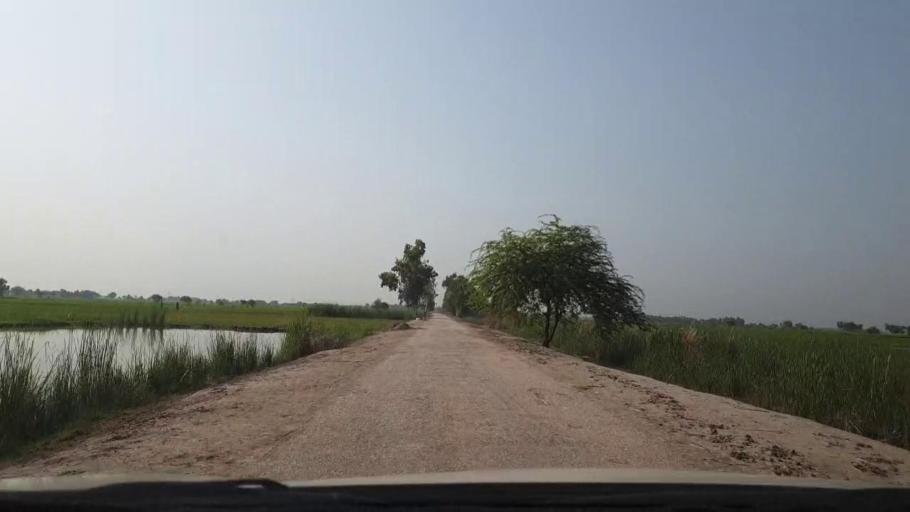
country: PK
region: Sindh
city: Goth Garelo
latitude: 27.4759
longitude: 68.0866
